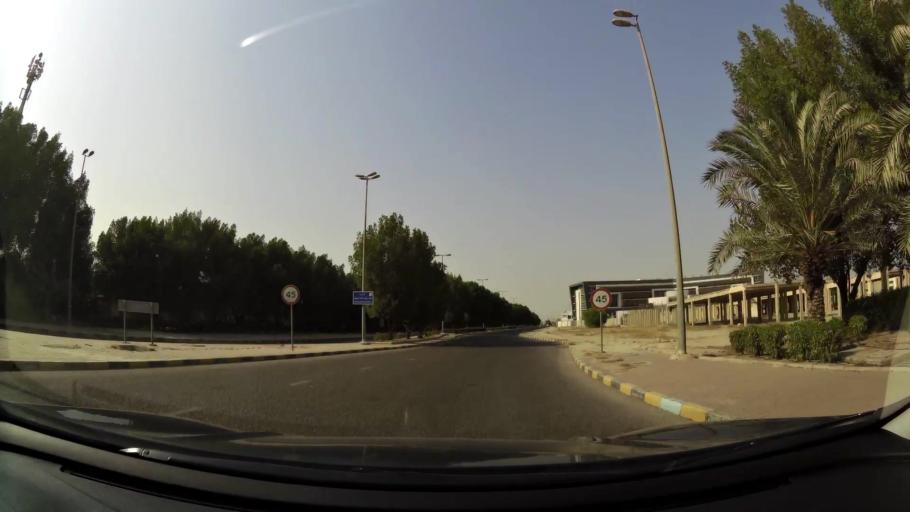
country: KW
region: Mubarak al Kabir
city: Sabah as Salim
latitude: 29.2672
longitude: 48.0529
